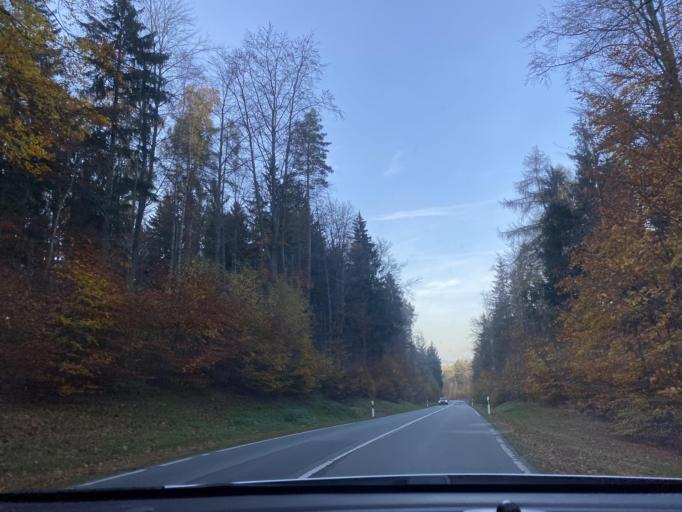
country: DE
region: Saxony
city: Olbersdorf
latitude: 50.8420
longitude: 14.7945
